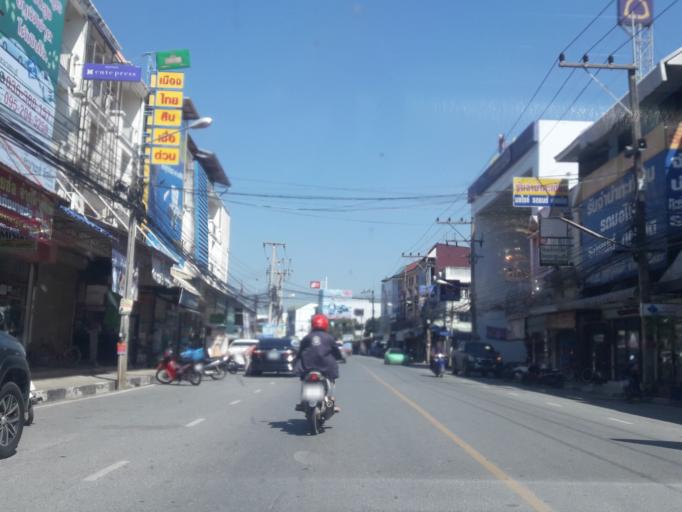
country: TH
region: Sara Buri
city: Nong Khae
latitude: 14.3433
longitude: 100.8671
